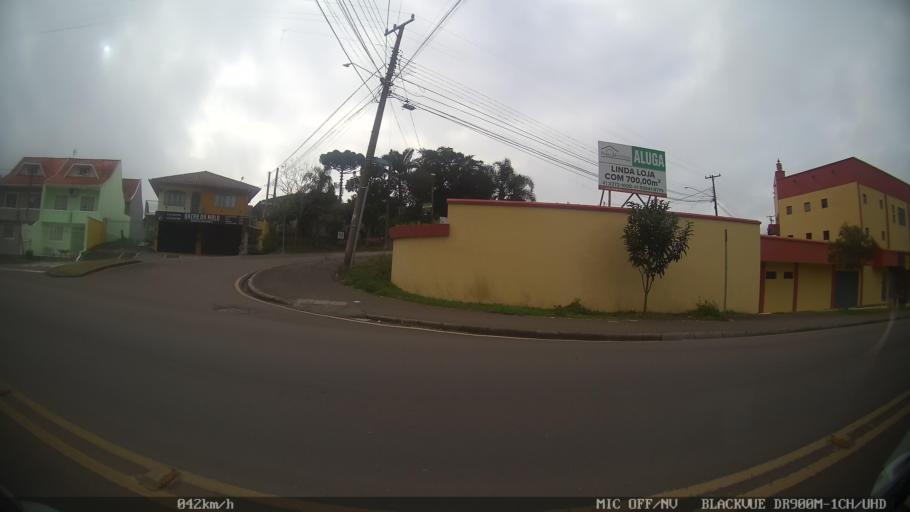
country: BR
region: Parana
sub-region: Almirante Tamandare
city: Almirante Tamandare
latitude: -25.3835
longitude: -49.3347
